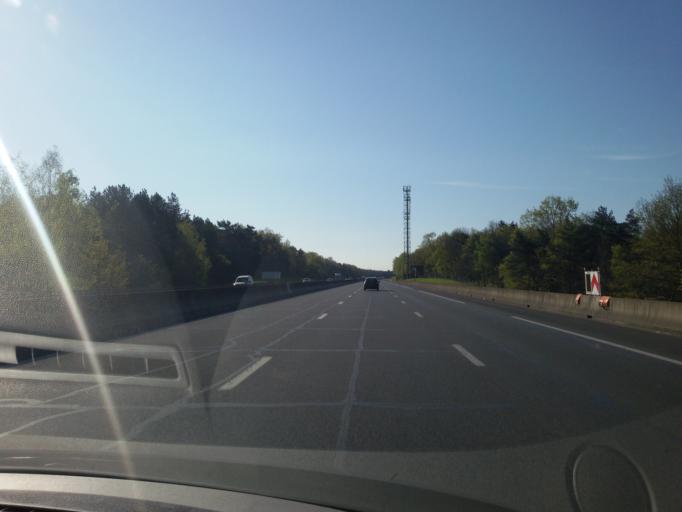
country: FR
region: Ile-de-France
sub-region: Departement de Seine-et-Marne
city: Bagneaux-sur-Loing
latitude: 48.2493
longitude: 2.7376
